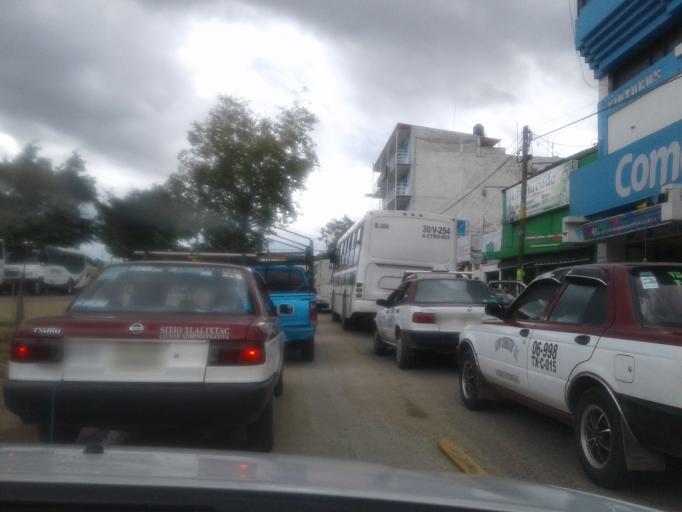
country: MX
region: Oaxaca
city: Oaxaca de Juarez
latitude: 17.0594
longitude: -96.7325
